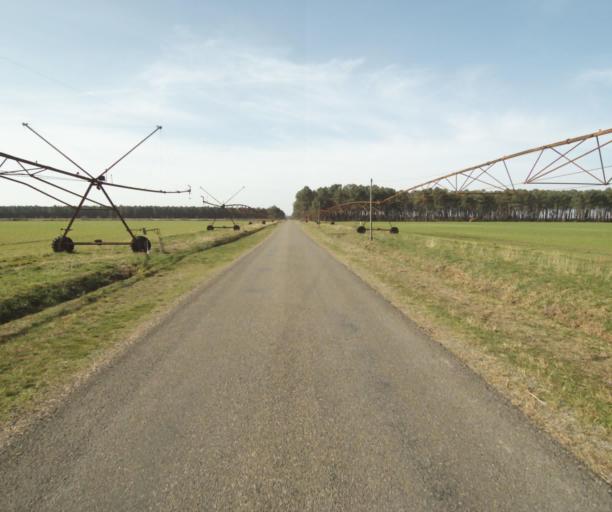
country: FR
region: Aquitaine
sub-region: Departement des Landes
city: Roquefort
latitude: 44.1815
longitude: -0.2180
